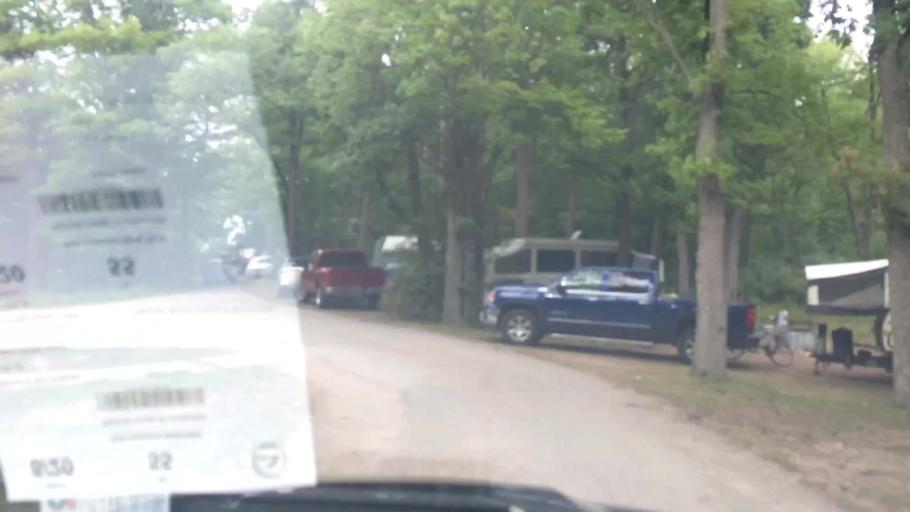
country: US
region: Michigan
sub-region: Huron County
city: Bad Axe
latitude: 44.0122
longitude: -83.0496
